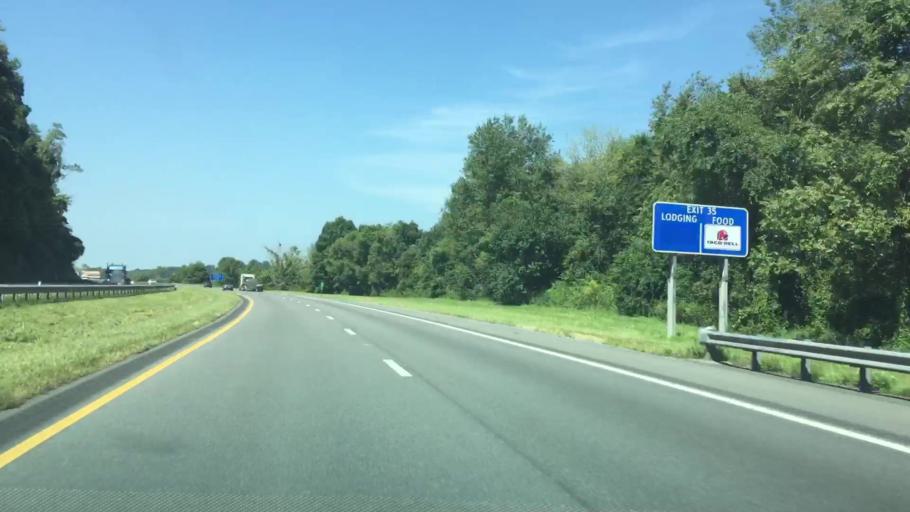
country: US
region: Virginia
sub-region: Smyth County
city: Chilhowie
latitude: 36.8086
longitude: -81.6561
